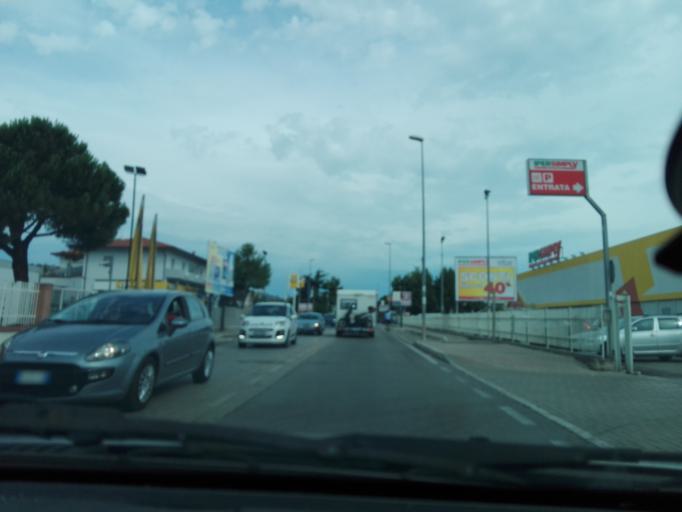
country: IT
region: Abruzzo
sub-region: Provincia di Pescara
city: San Martino Bassa
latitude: 42.5341
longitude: 14.1296
